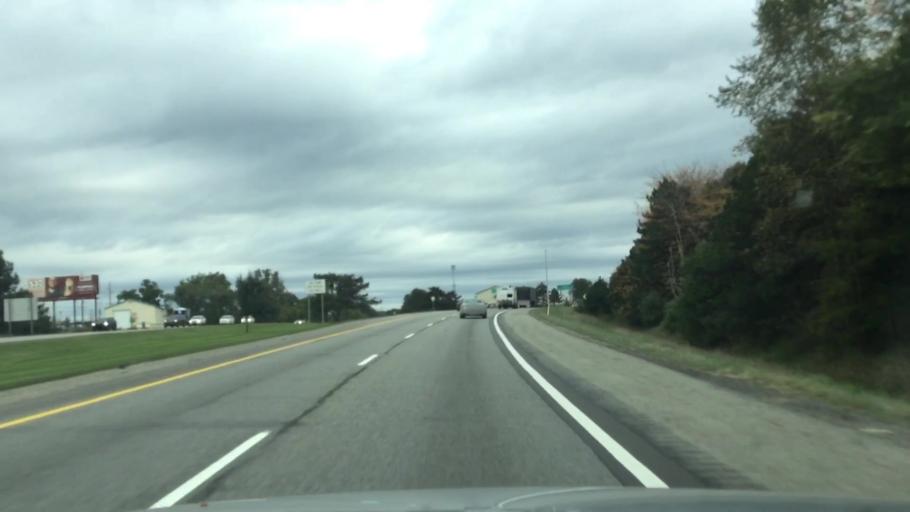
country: US
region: Michigan
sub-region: Livingston County
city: Brighton
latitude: 42.5143
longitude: -83.7580
